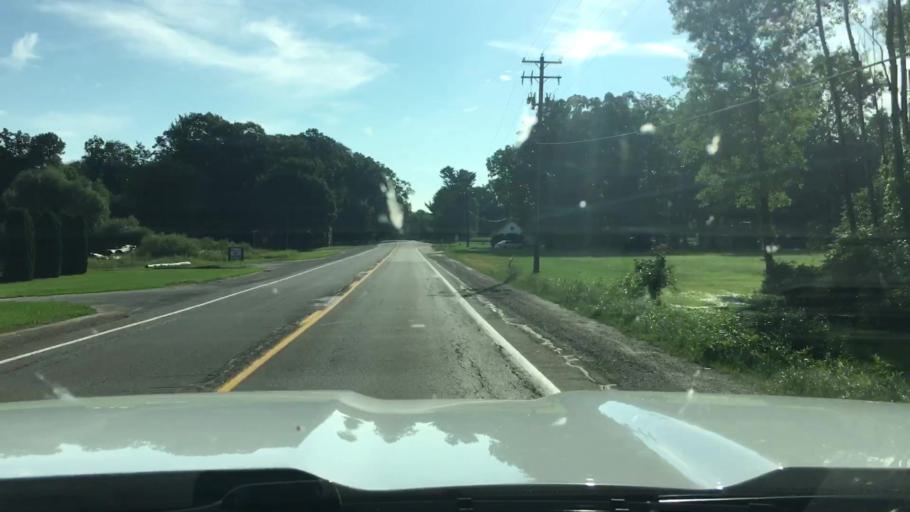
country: US
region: Michigan
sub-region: Kent County
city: Cedar Springs
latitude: 43.2194
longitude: -85.6381
